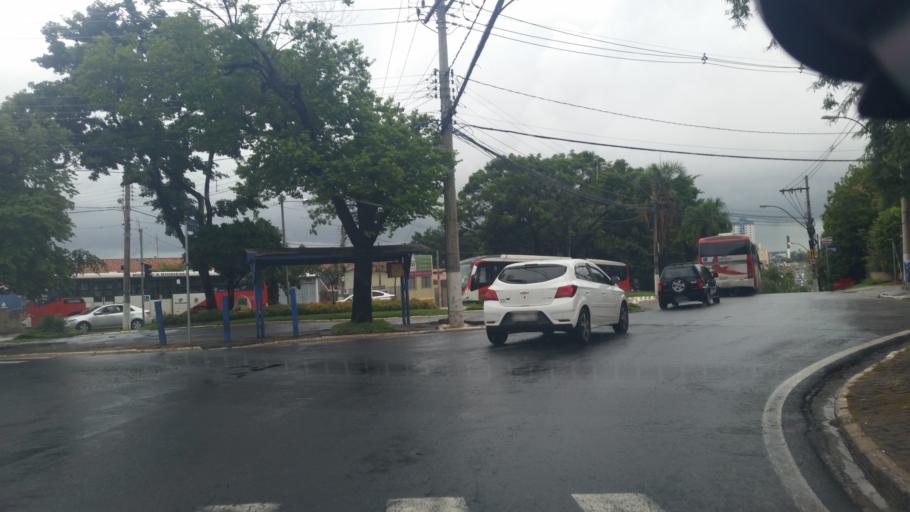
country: BR
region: Sao Paulo
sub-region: Campinas
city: Campinas
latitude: -22.9084
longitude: -47.0869
